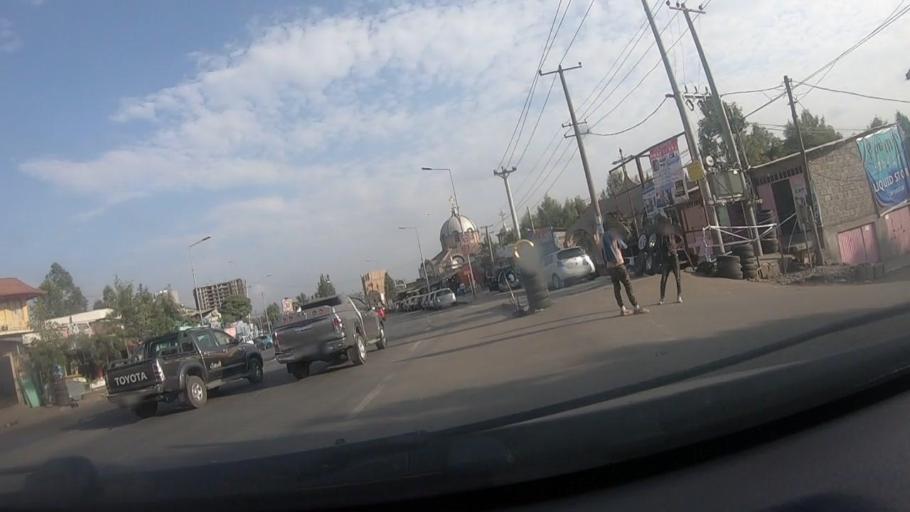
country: ET
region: Adis Abeba
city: Addis Ababa
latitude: 8.9829
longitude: 38.7275
